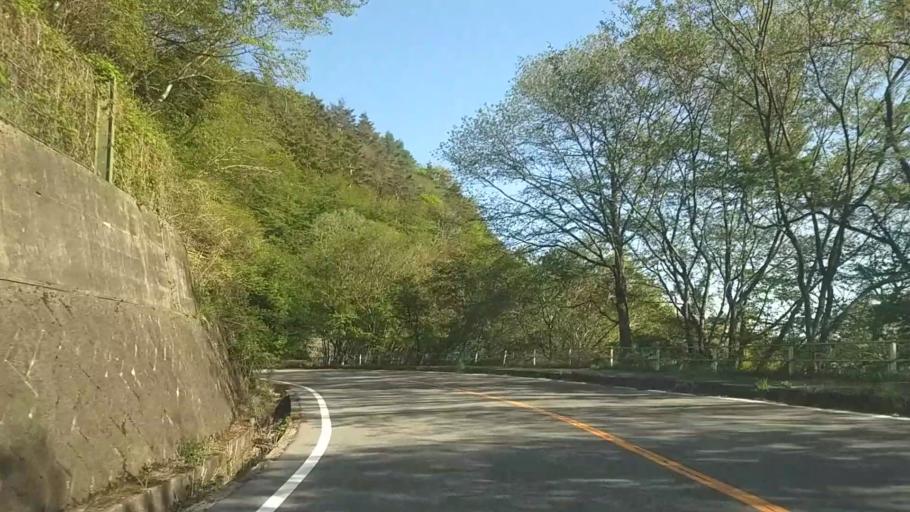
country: JP
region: Yamanashi
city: Nirasaki
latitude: 35.9059
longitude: 138.3813
